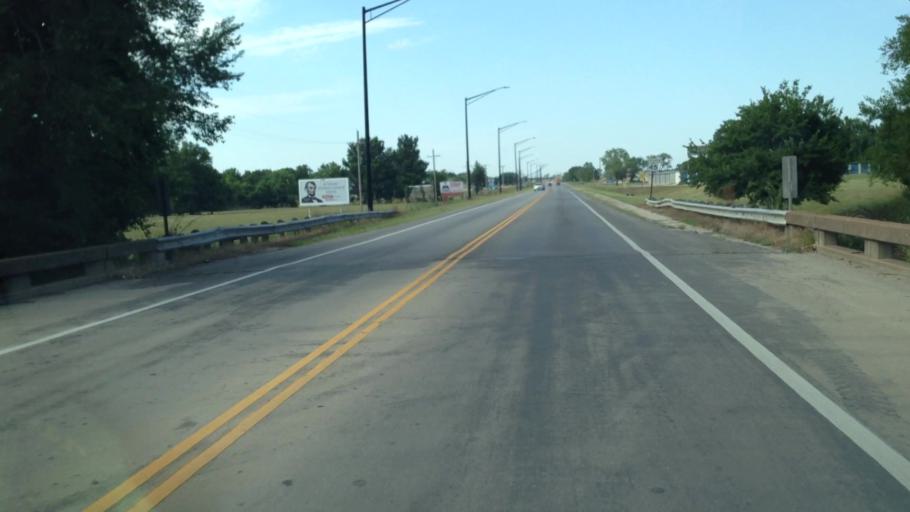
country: US
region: Kansas
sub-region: Labette County
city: Parsons
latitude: 37.3513
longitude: -95.2590
